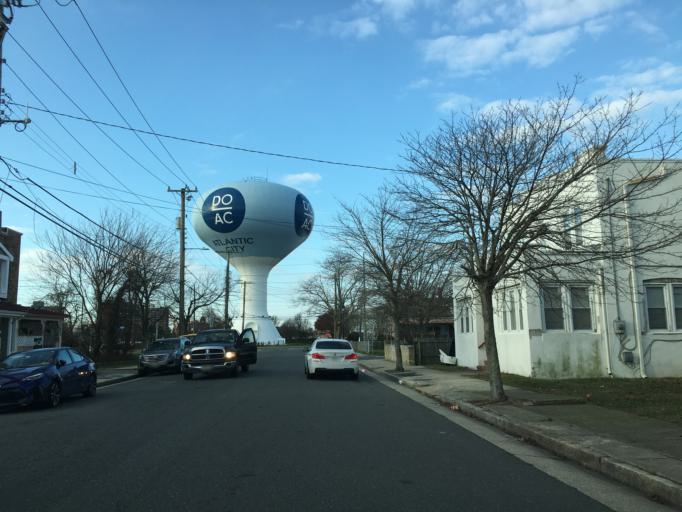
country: US
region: New Jersey
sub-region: Atlantic County
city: Atlantic City
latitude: 39.3706
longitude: -74.4244
